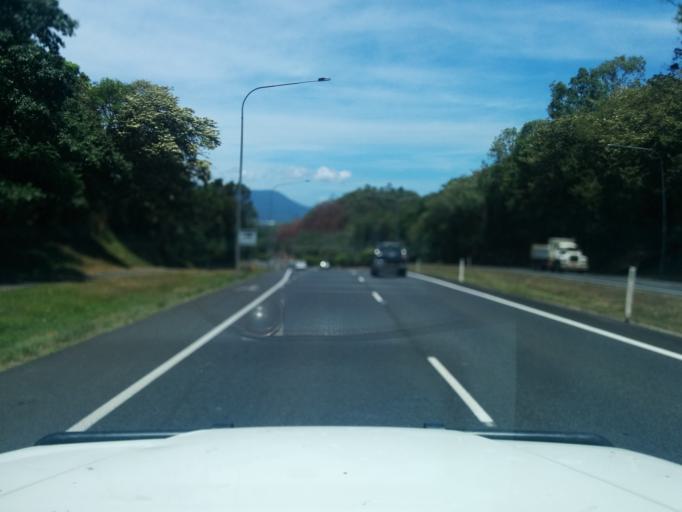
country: AU
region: Queensland
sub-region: Cairns
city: Redlynch
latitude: -16.9137
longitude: 145.7236
